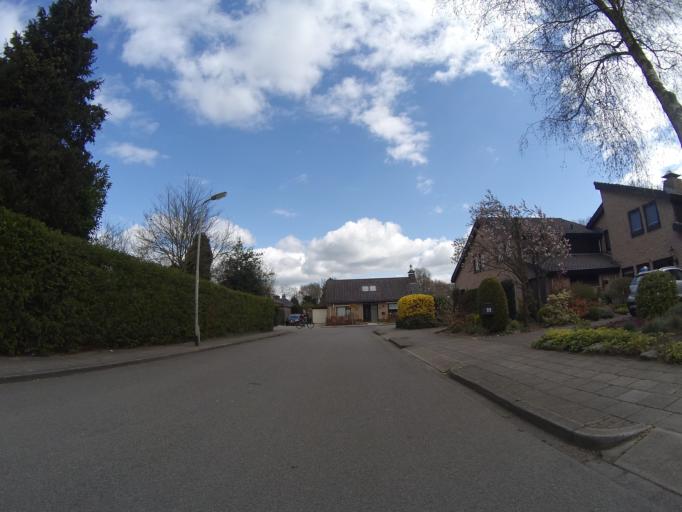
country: NL
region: Utrecht
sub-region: Gemeente Amersfoort
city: Randenbroek
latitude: 52.1397
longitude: 5.3988
